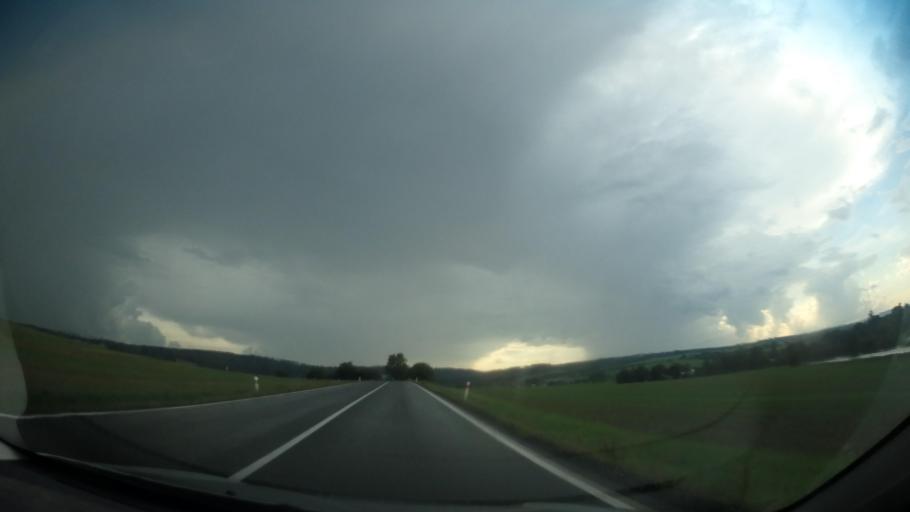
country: CZ
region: Olomoucky
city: Bila Lhota
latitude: 49.7082
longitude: 16.9830
